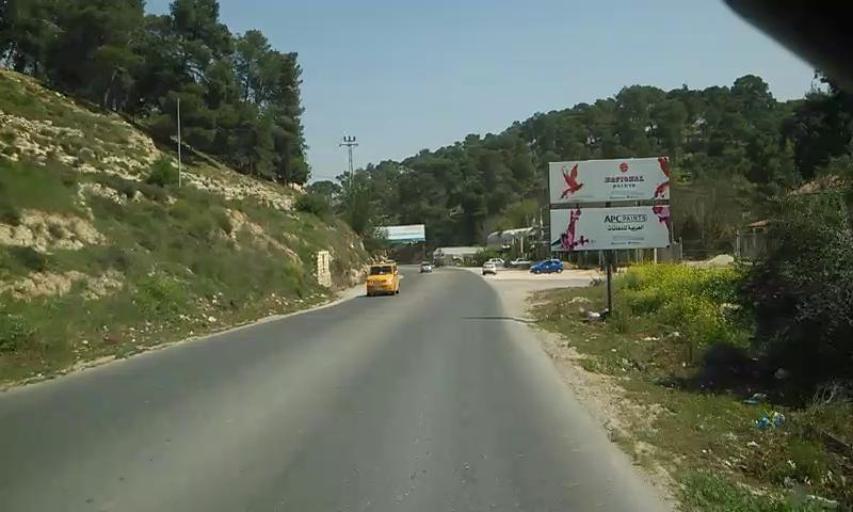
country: PS
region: West Bank
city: Ash Shuhada'
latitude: 32.4403
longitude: 35.2867
